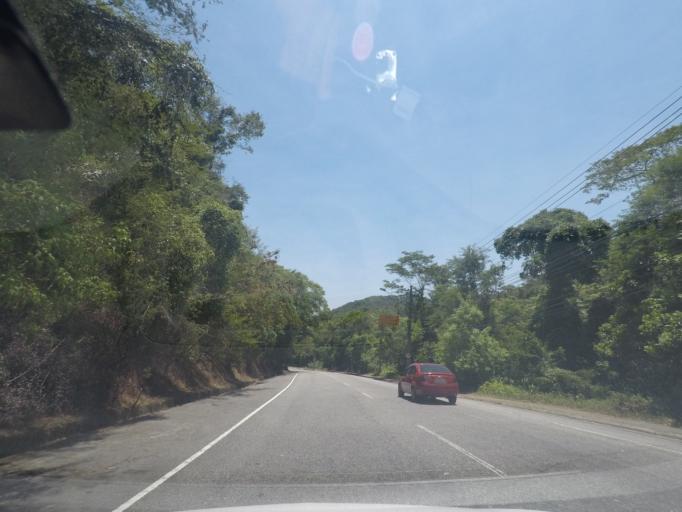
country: BR
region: Rio de Janeiro
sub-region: Niteroi
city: Niteroi
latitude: -22.9207
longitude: -43.0651
